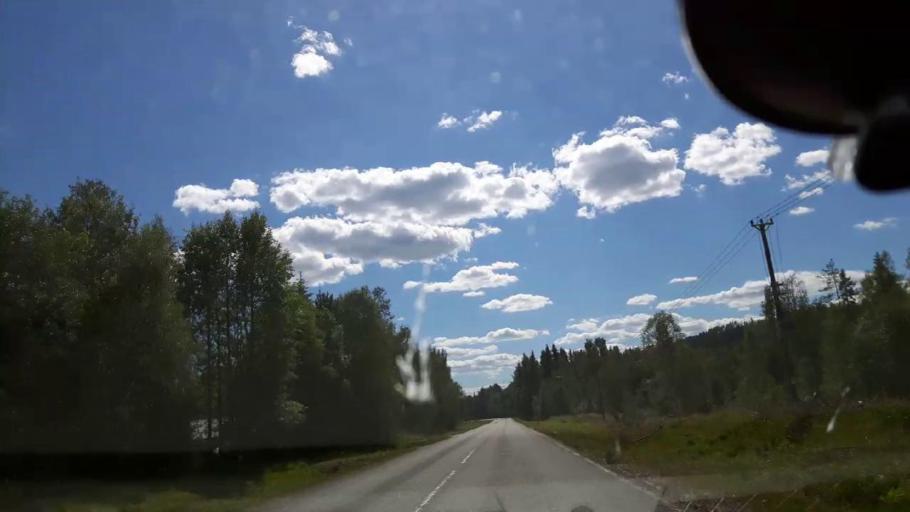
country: SE
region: Jaemtland
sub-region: Ragunda Kommun
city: Hammarstrand
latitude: 62.8826
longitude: 16.2243
